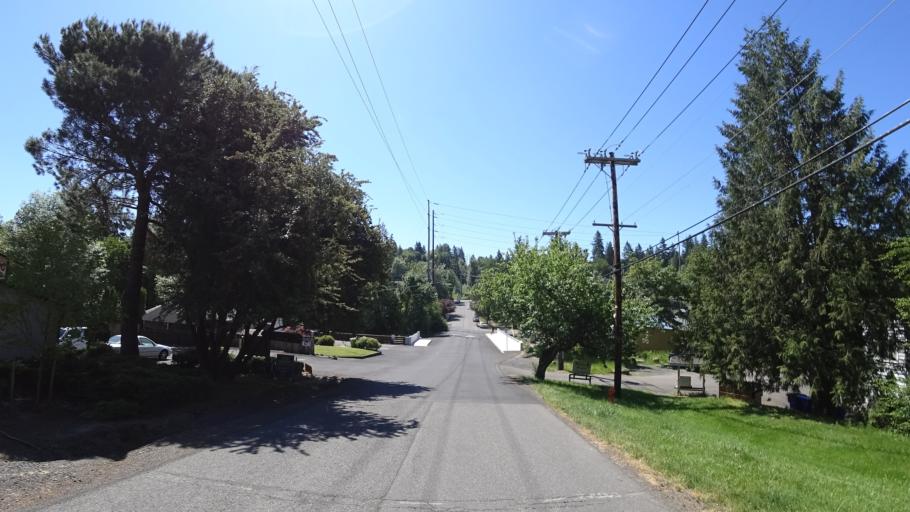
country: US
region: Oregon
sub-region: Washington County
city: Raleigh Hills
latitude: 45.4875
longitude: -122.7233
